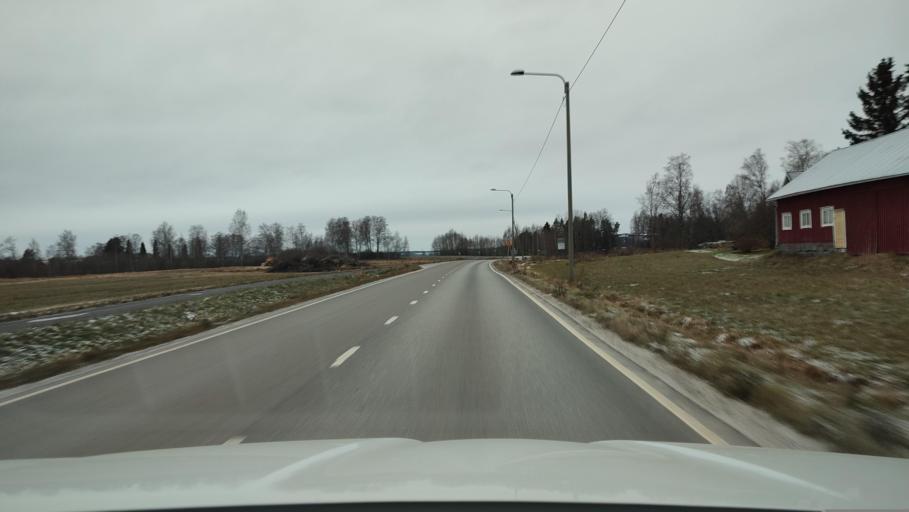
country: FI
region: Ostrobothnia
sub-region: Vaasa
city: Ristinummi
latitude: 63.0351
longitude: 21.7869
